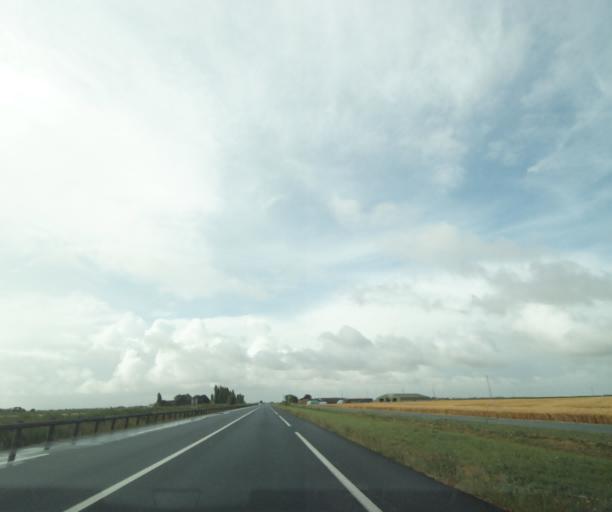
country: FR
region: Pays de la Loire
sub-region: Departement de la Vendee
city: Champagne-les-Marais
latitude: 46.3535
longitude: -1.0860
